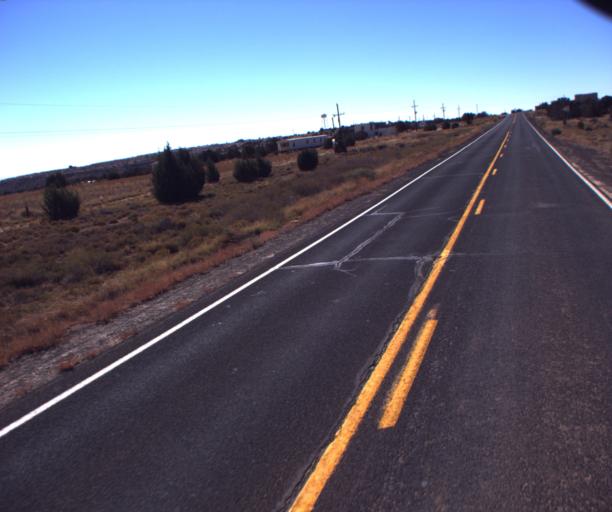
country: US
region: Arizona
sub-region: Navajo County
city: First Mesa
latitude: 35.8323
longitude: -110.5300
